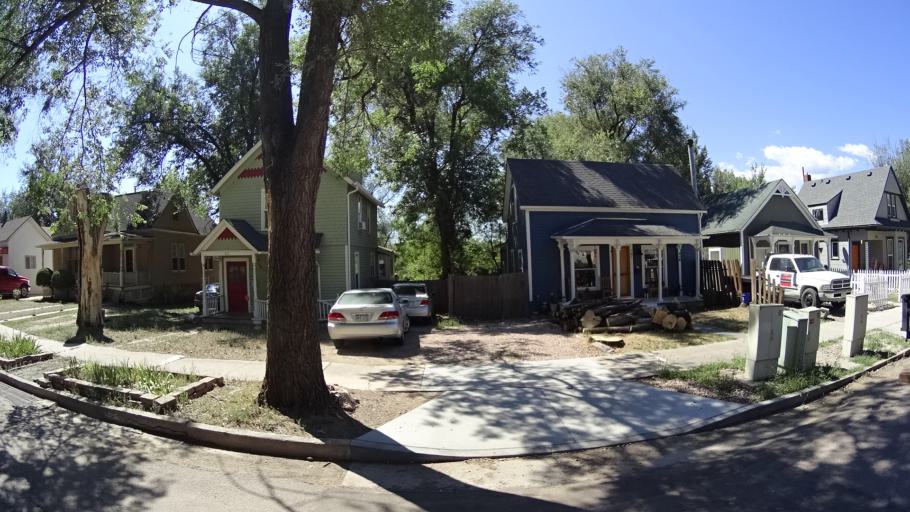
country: US
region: Colorado
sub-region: El Paso County
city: Colorado Springs
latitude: 38.8349
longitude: -104.8125
